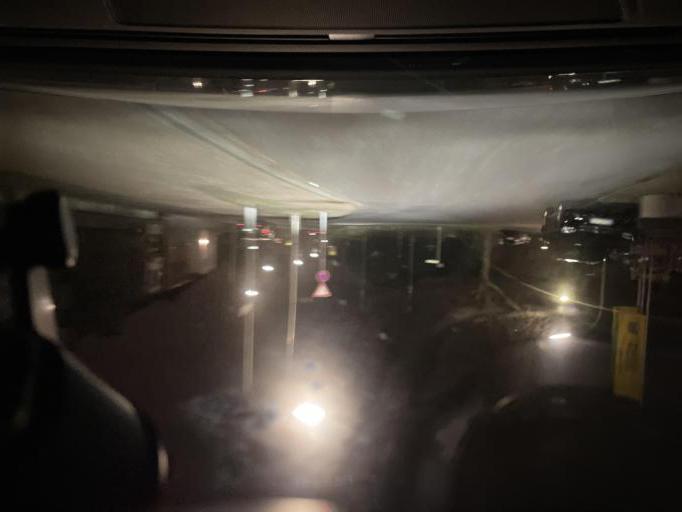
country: DE
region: North Rhine-Westphalia
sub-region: Regierungsbezirk Dusseldorf
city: Korschenbroich
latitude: 51.2283
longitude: 6.4803
